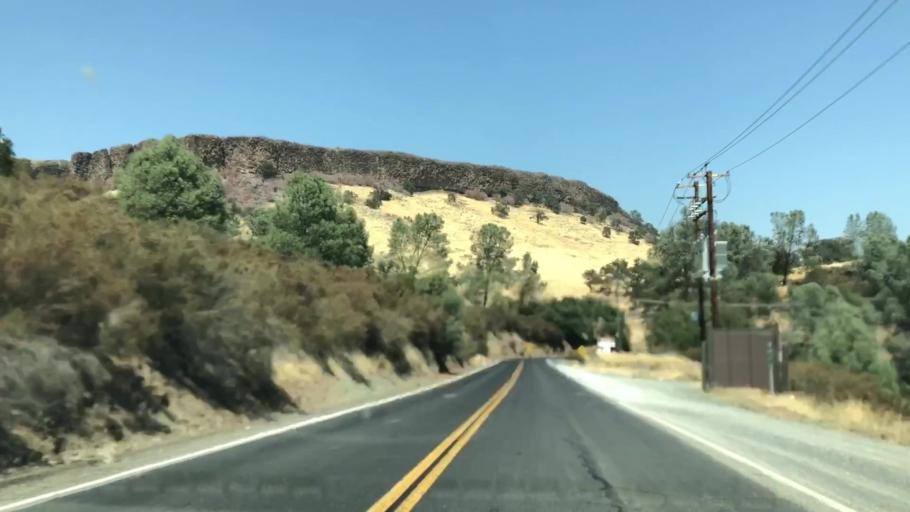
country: US
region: California
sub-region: Calaveras County
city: Copperopolis
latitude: 37.8980
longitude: -120.5718
